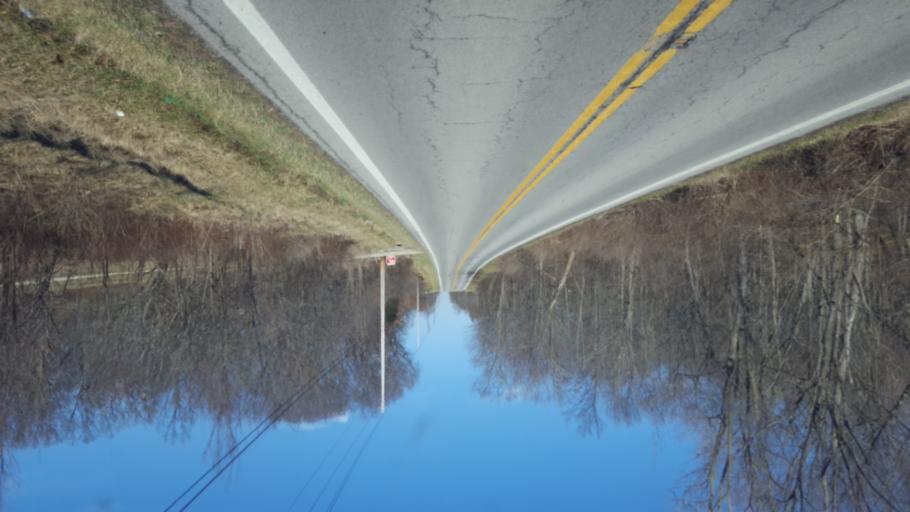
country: US
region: Ohio
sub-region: Marion County
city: Prospect
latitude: 40.4962
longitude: -83.1904
